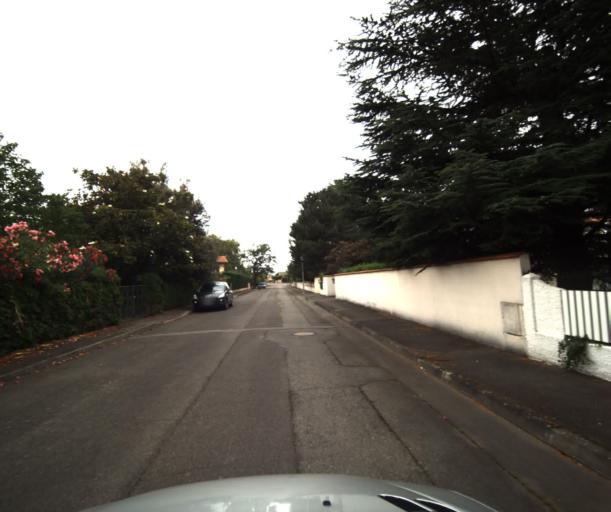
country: FR
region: Midi-Pyrenees
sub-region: Departement de la Haute-Garonne
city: Lacroix-Falgarde
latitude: 43.4910
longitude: 1.3990
